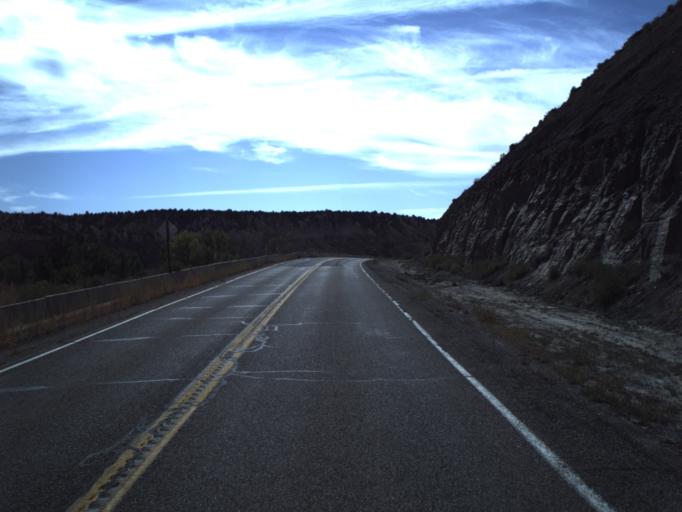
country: US
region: Utah
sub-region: Garfield County
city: Panguitch
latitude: 37.6100
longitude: -112.0618
